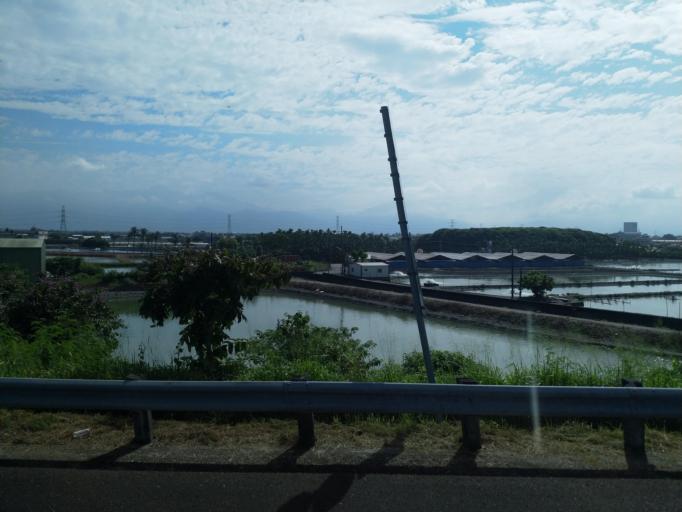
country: TW
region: Taiwan
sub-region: Pingtung
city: Pingtung
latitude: 22.8130
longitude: 120.4858
